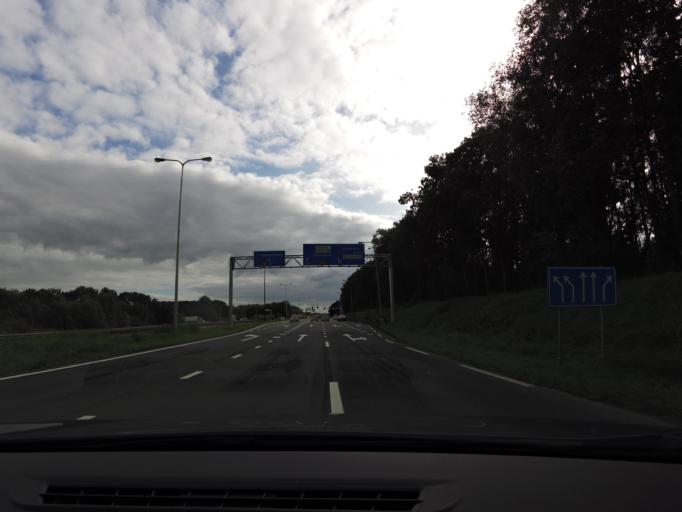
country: NL
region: Utrecht
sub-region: Gemeente IJsselstein
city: IJsselstein
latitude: 52.0225
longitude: 5.0612
